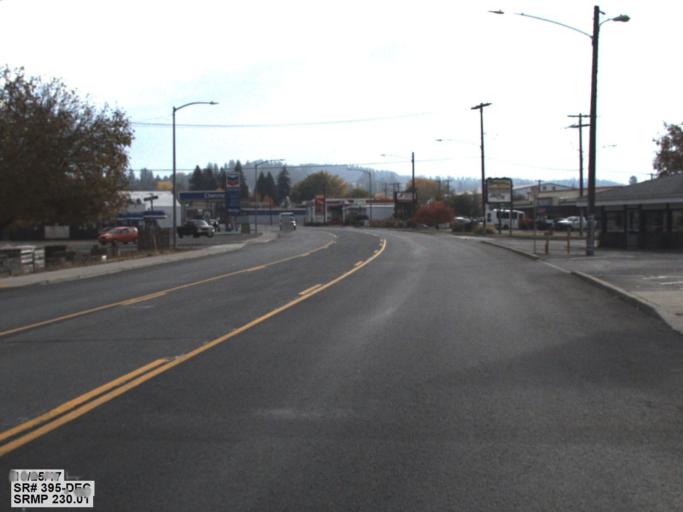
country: US
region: Washington
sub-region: Stevens County
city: Colville
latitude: 48.5491
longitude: -117.9112
